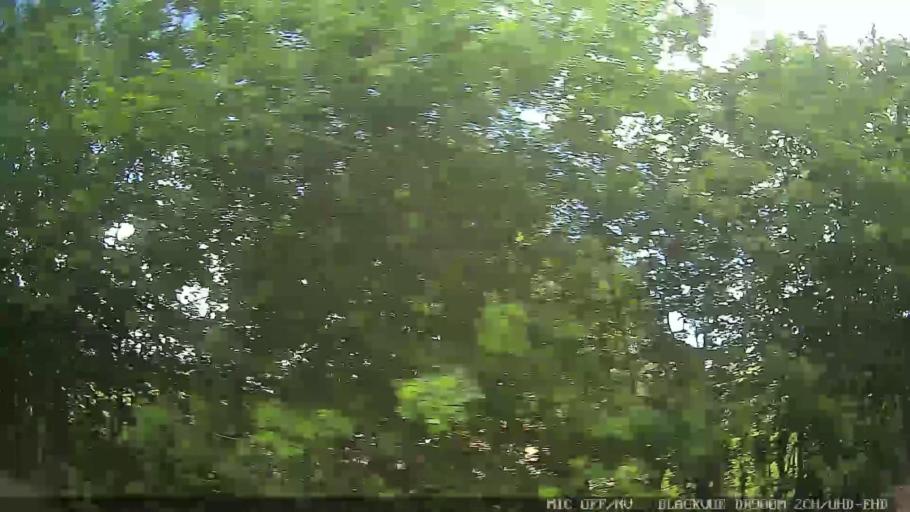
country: BR
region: Sao Paulo
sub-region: Conchas
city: Conchas
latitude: -22.9829
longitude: -47.9903
